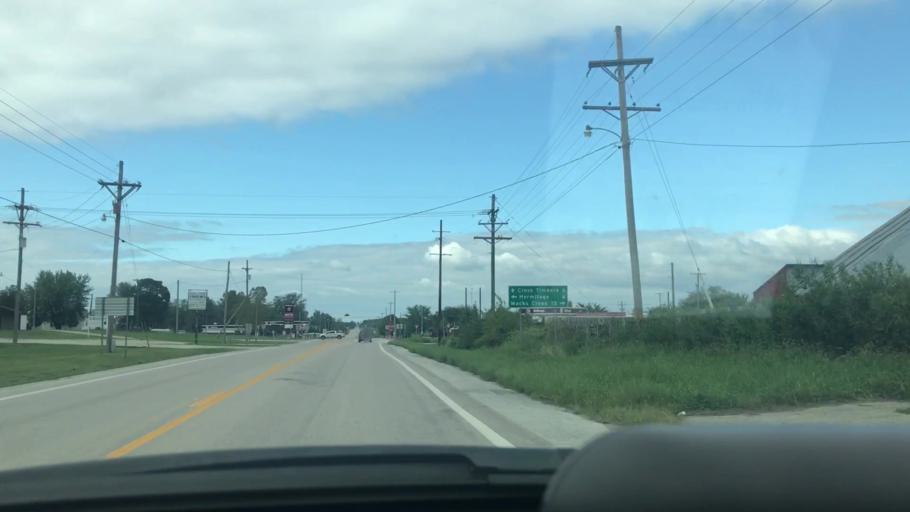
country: US
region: Missouri
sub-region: Hickory County
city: Hermitage
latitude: 37.9392
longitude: -93.2081
